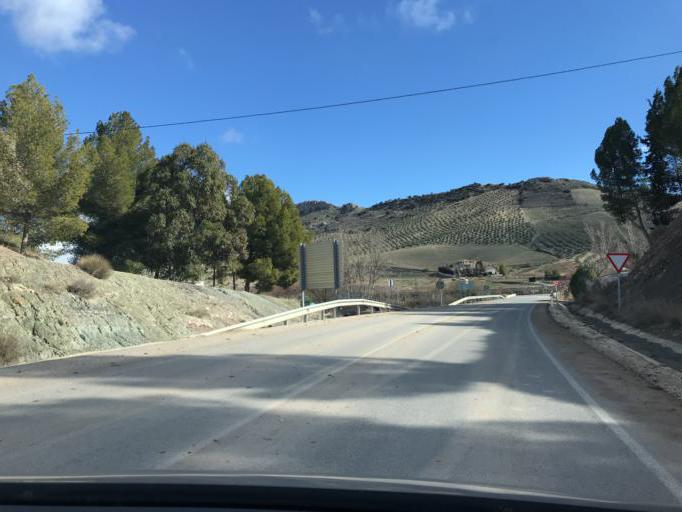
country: ES
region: Andalusia
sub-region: Provincia de Jaen
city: Huelma
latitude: 37.6494
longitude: -3.4229
